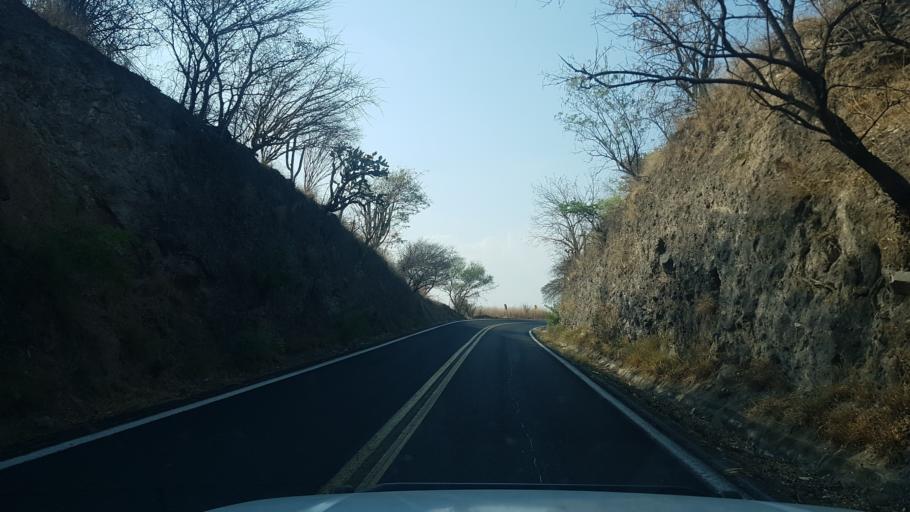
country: MX
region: Puebla
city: Calmeca
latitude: 18.6526
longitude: -98.6642
